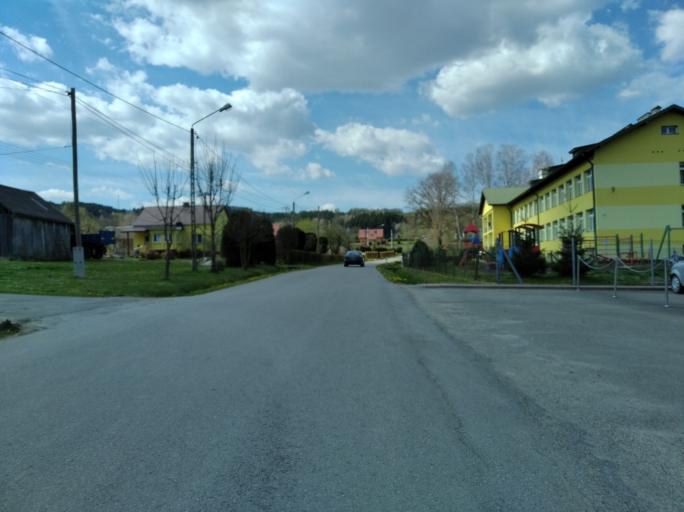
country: PL
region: Subcarpathian Voivodeship
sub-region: Powiat brzozowski
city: Wesola
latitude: 49.7786
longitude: 22.1344
